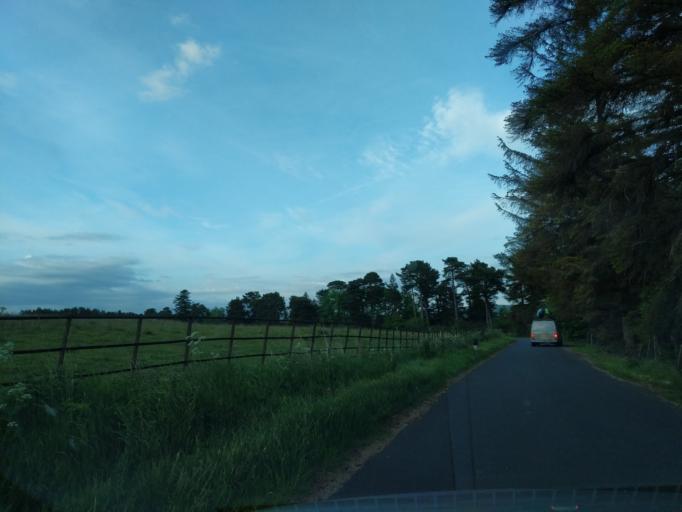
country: GB
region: Scotland
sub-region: Midlothian
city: Bonnyrigg
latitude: 55.7747
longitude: -3.1238
